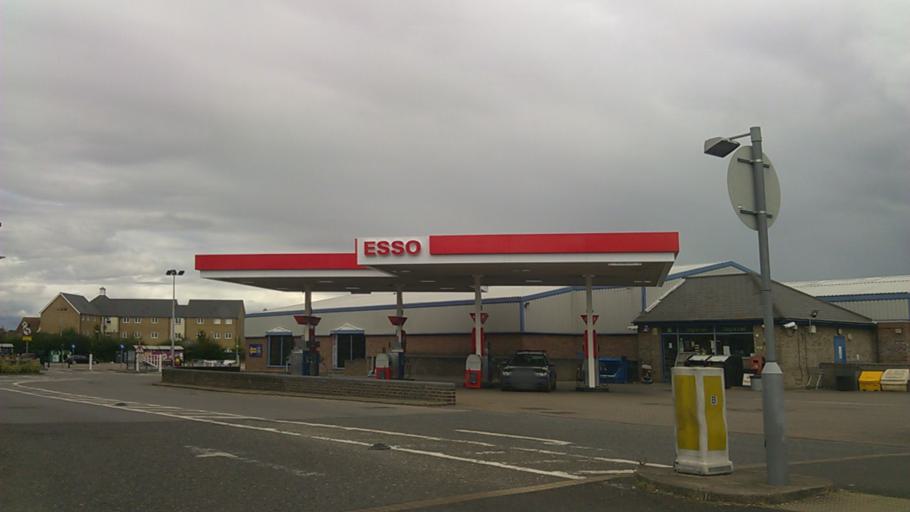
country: GB
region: England
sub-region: Essex
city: Eight Ash Green
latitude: 51.8778
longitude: 0.8455
